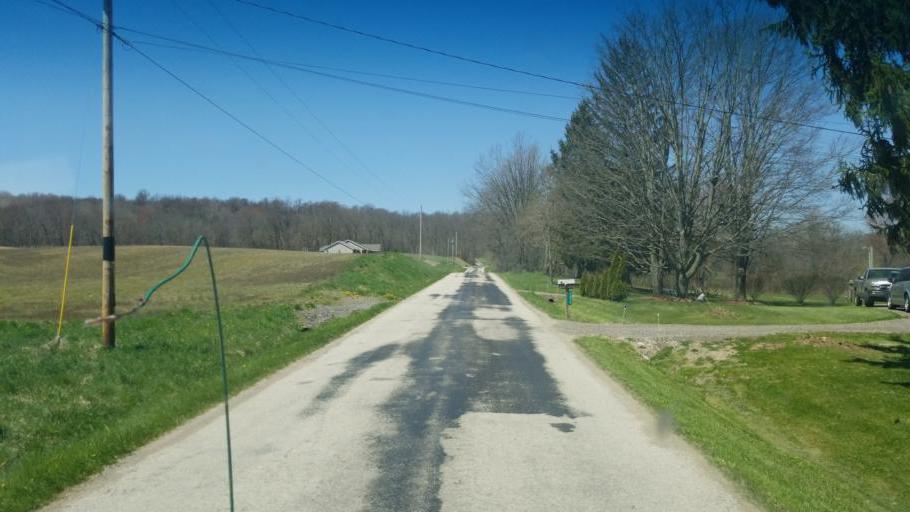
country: US
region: Ohio
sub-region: Richland County
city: Lincoln Heights
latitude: 40.8513
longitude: -82.4388
